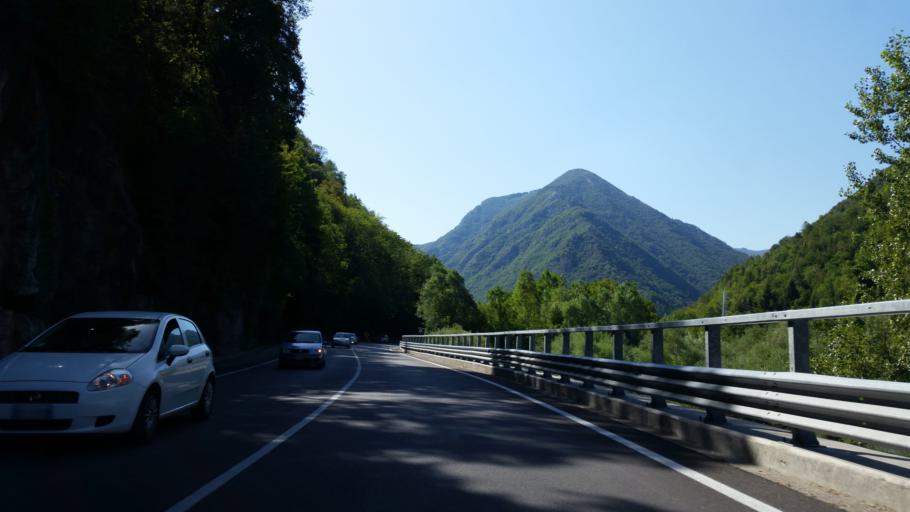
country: IT
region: Piedmont
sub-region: Provincia di Cuneo
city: Vernante
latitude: 44.2534
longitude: 7.5291
